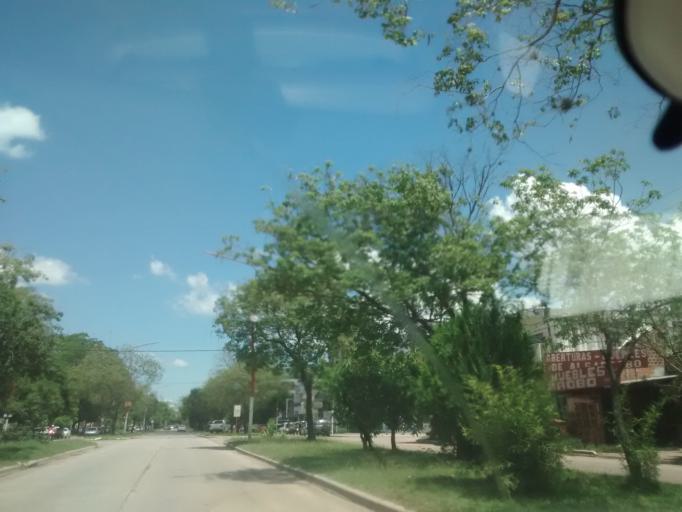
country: AR
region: Chaco
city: Resistencia
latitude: -27.4563
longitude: -58.9949
